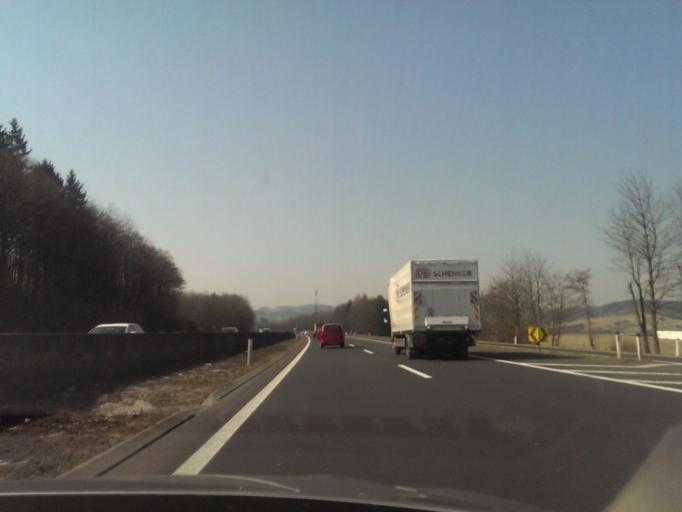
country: AT
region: Upper Austria
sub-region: Politischer Bezirk Grieskirchen
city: Bad Schallerbach
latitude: 48.1890
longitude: 13.9342
